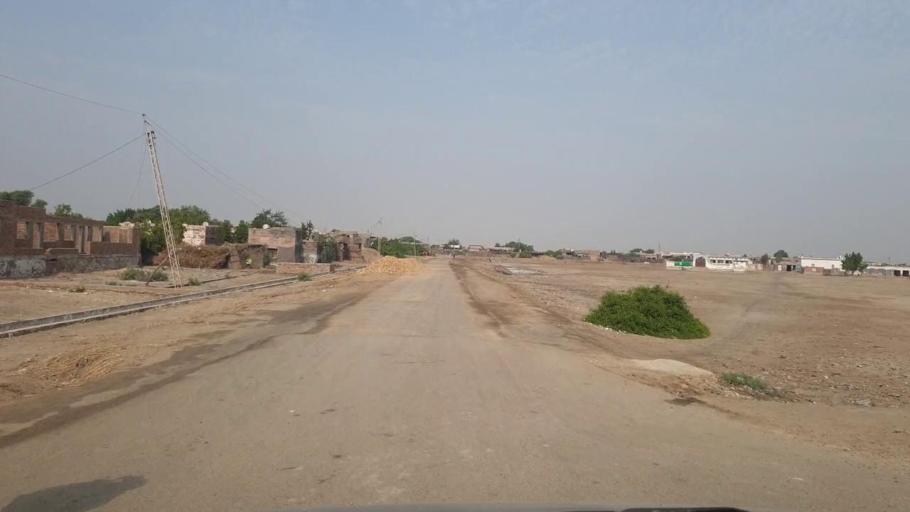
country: PK
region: Sindh
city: Tando Muhammad Khan
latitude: 25.1347
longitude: 68.4532
